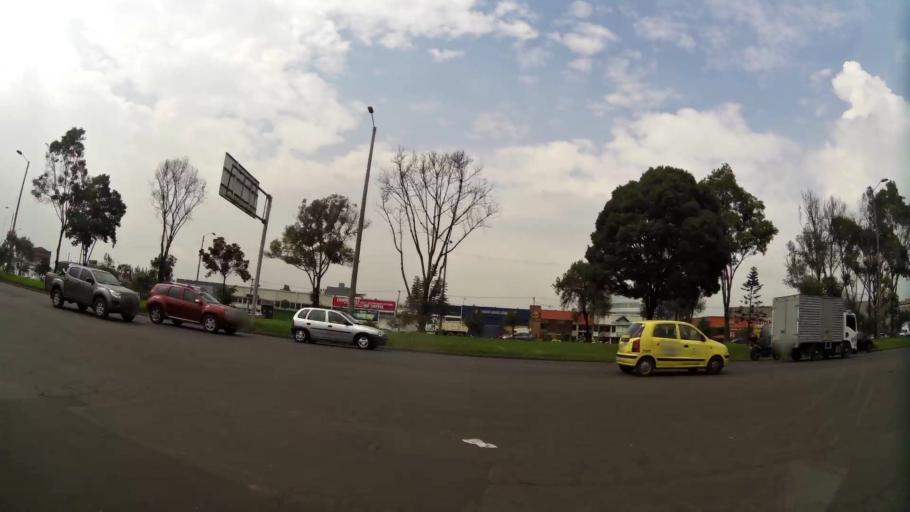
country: CO
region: Bogota D.C.
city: Bogota
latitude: 4.6257
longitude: -74.0949
